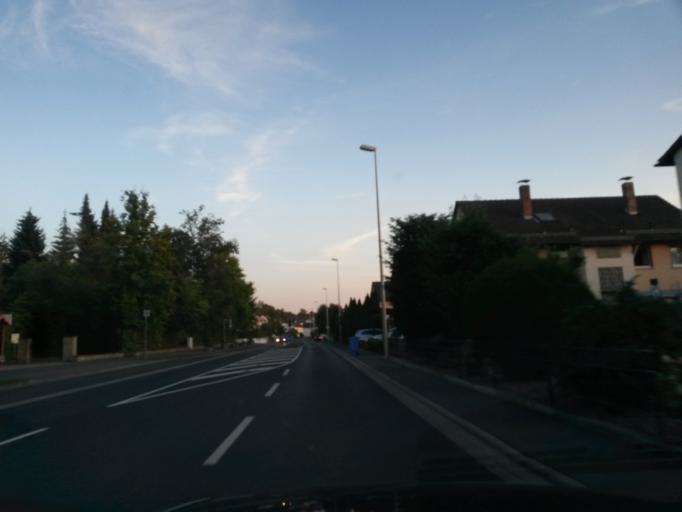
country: DE
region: Bavaria
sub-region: Regierungsbezirk Unterfranken
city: Marktheidenfeld
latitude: 49.8445
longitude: 9.6129
